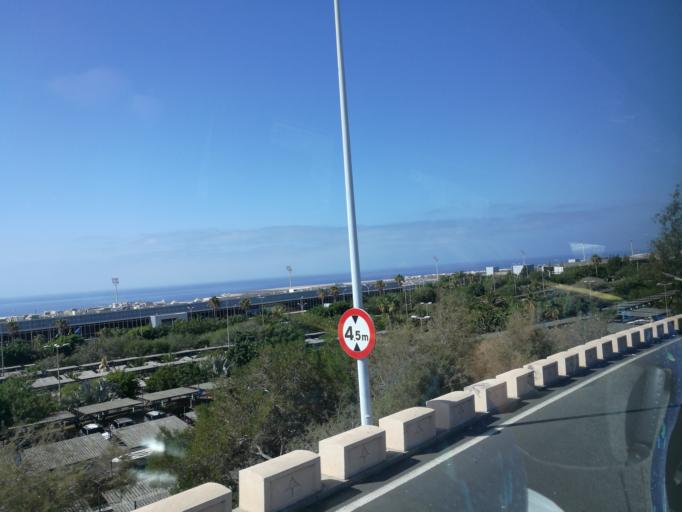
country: ES
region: Canary Islands
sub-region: Provincia de Santa Cruz de Tenerife
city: San Isidro
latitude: 28.0497
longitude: -16.5787
